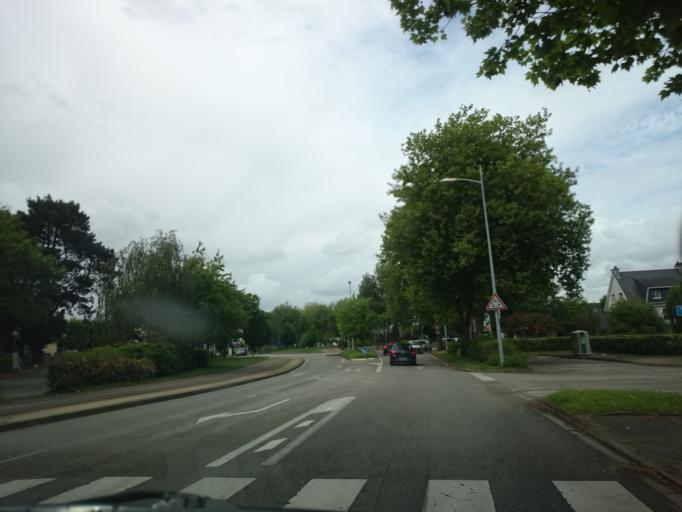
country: FR
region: Brittany
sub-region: Departement du Morbihan
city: Vannes
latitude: 47.6587
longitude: -2.7810
